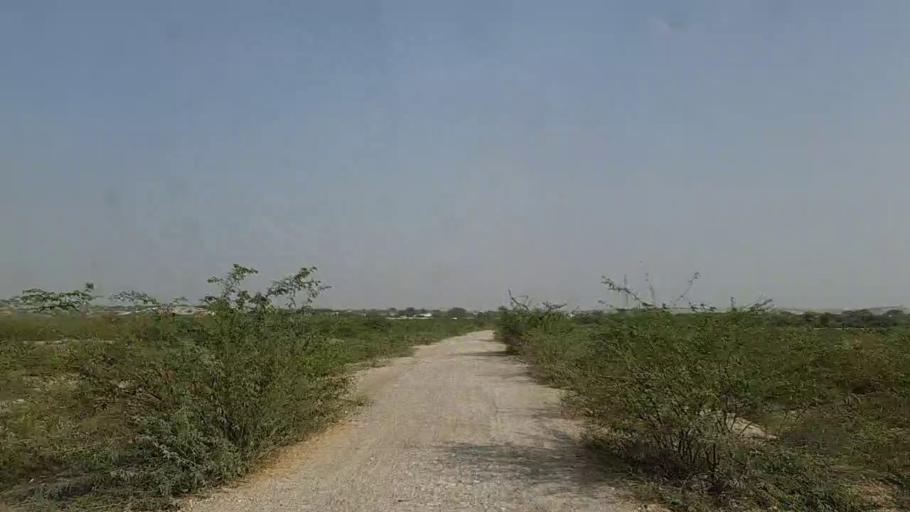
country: PK
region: Sindh
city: Naukot
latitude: 24.6624
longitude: 69.2842
